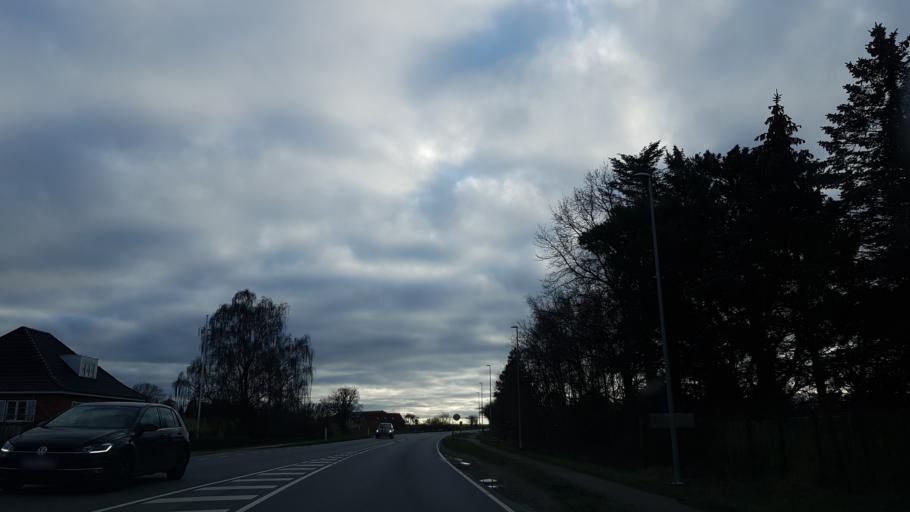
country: DK
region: Zealand
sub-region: Kalundborg Kommune
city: Hong
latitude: 55.4876
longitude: 11.2962
